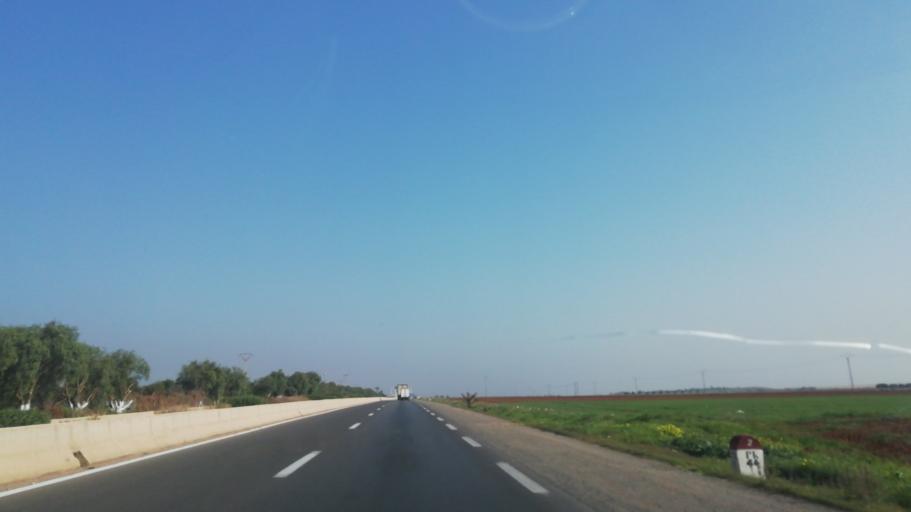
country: DZ
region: Ain Temouchent
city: El Amria
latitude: 35.5425
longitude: -0.9717
